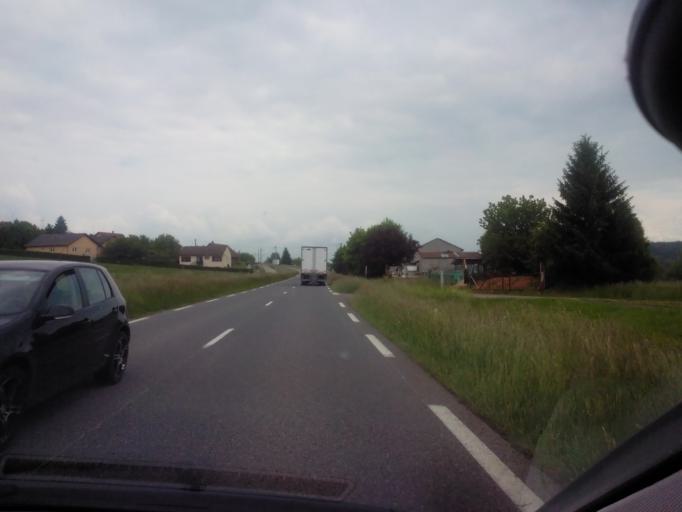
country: FR
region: Lorraine
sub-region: Departement de la Moselle
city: Sarrebourg
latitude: 48.7798
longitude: 7.0526
